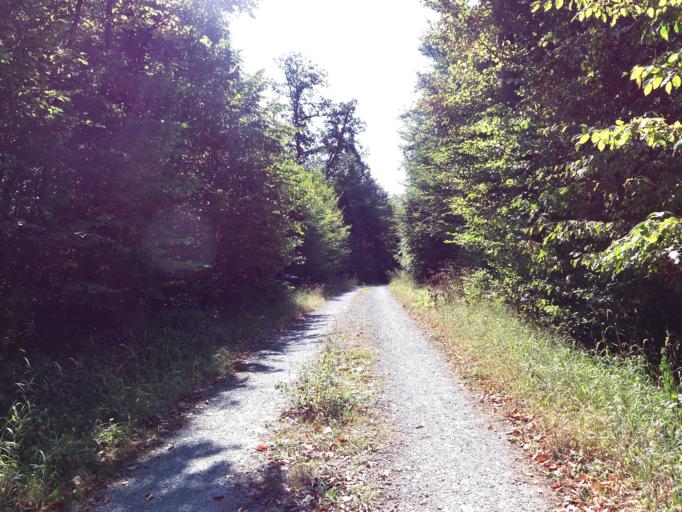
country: DE
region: Bavaria
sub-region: Regierungsbezirk Unterfranken
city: Wuerzburg
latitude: 49.7637
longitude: 9.9011
